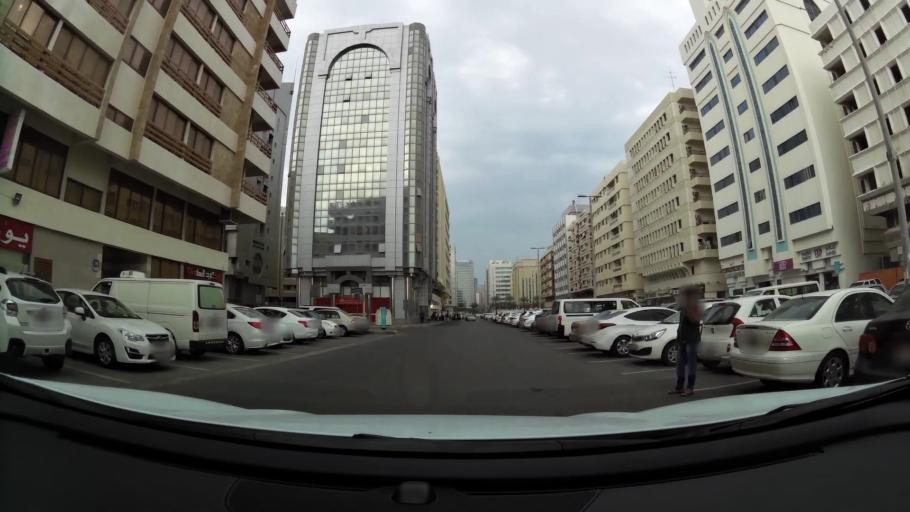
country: AE
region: Abu Dhabi
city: Abu Dhabi
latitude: 24.4885
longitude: 54.3821
